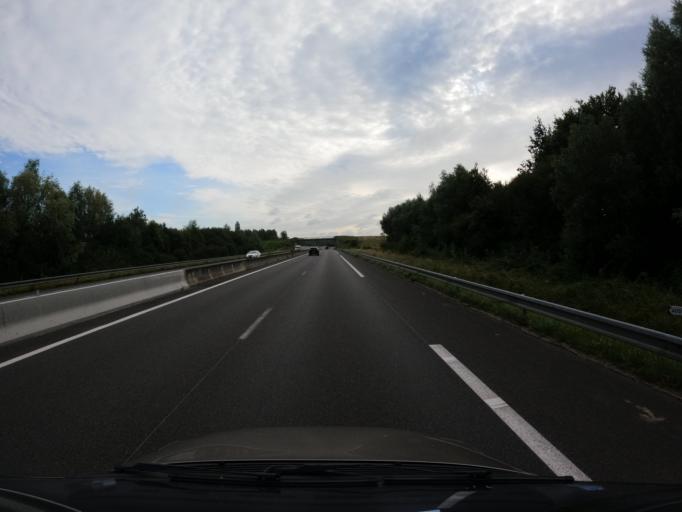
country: FR
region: Centre
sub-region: Departement d'Indre-et-Loire
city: Restigne
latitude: 47.2753
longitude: 0.2686
